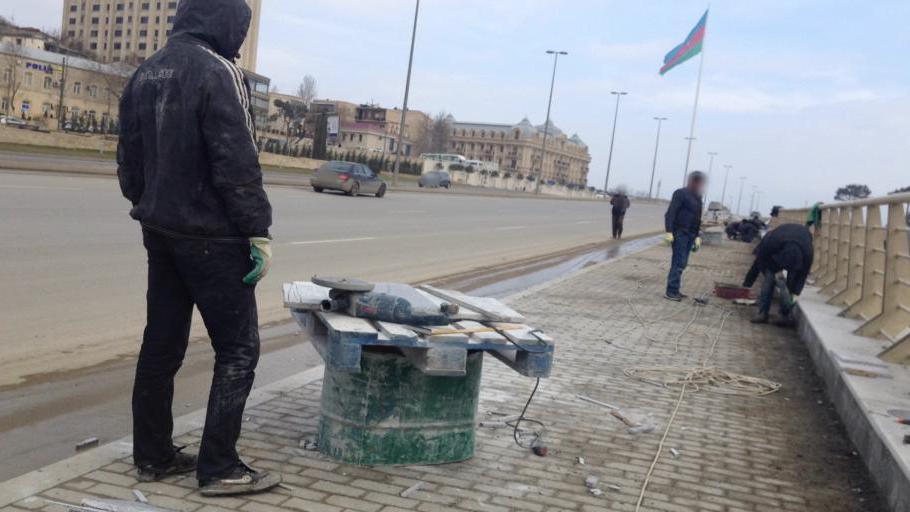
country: AZ
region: Baki
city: Badamdar
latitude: 40.3402
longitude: 49.8381
